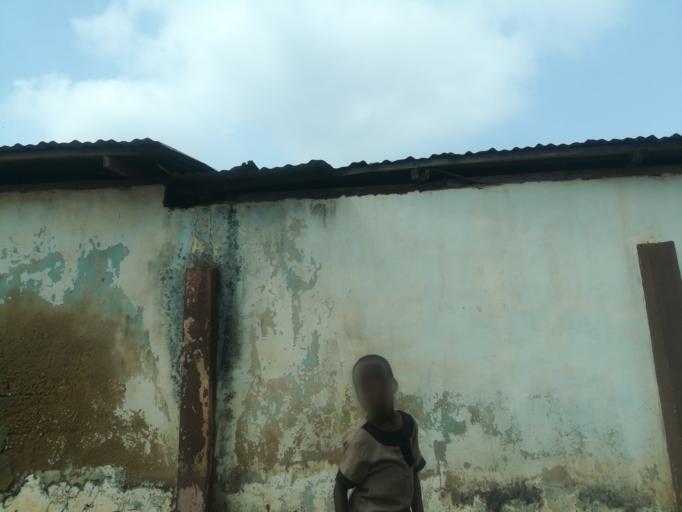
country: NG
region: Oyo
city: Ibadan
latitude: 7.4170
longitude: 3.9530
